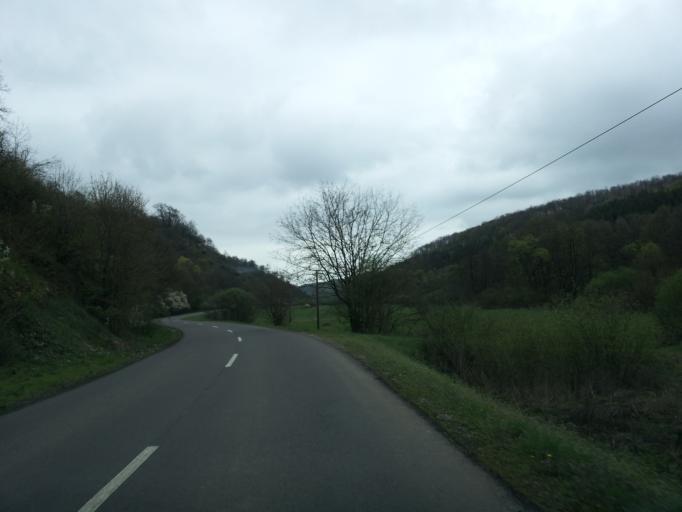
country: HU
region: Borsod-Abauj-Zemplen
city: Rudabanya
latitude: 48.4785
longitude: 20.5746
